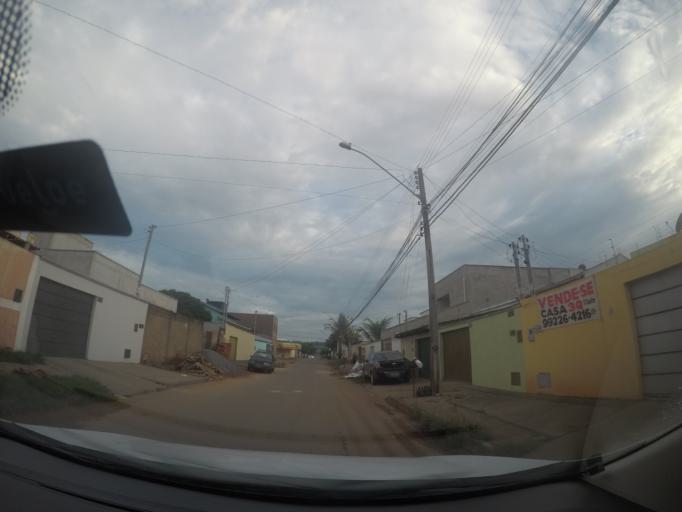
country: BR
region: Goias
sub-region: Goiania
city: Goiania
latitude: -16.6873
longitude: -49.3459
